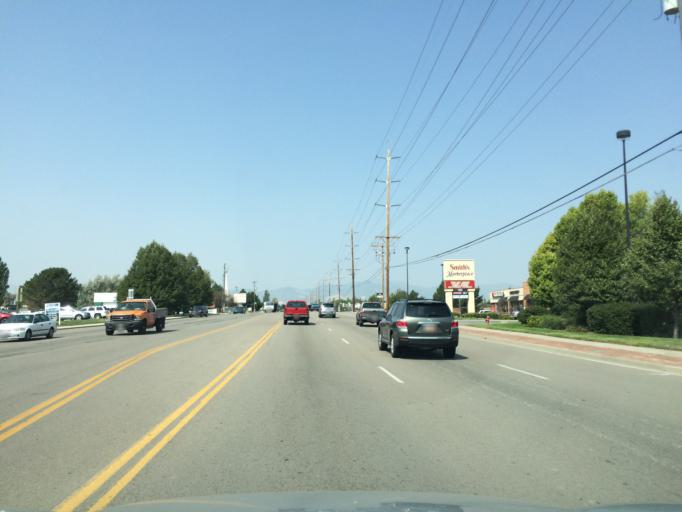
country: US
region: Utah
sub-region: Salt Lake County
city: West Jordan
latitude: 40.5878
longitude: -111.9397
